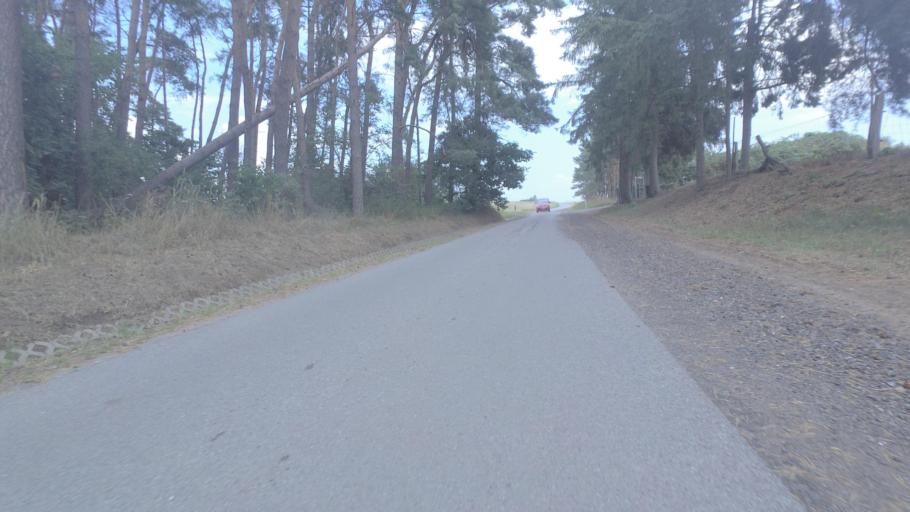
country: DE
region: Mecklenburg-Vorpommern
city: Borrentin
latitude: 53.8389
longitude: 12.9418
